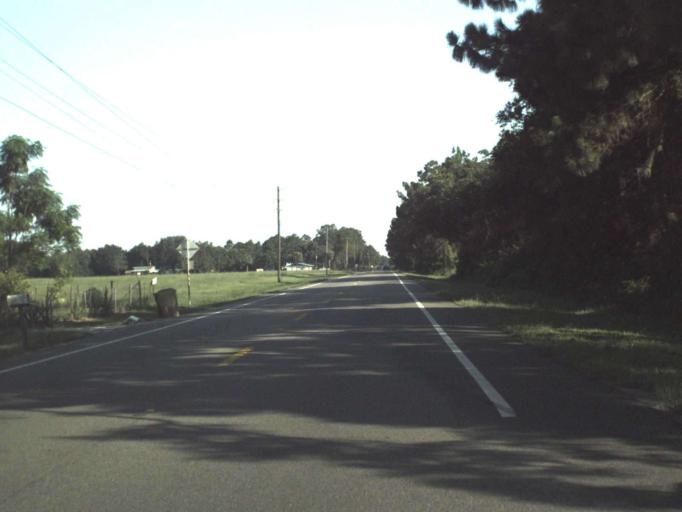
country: US
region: Florida
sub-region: Lake County
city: Clermont
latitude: 28.3908
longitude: -81.8256
